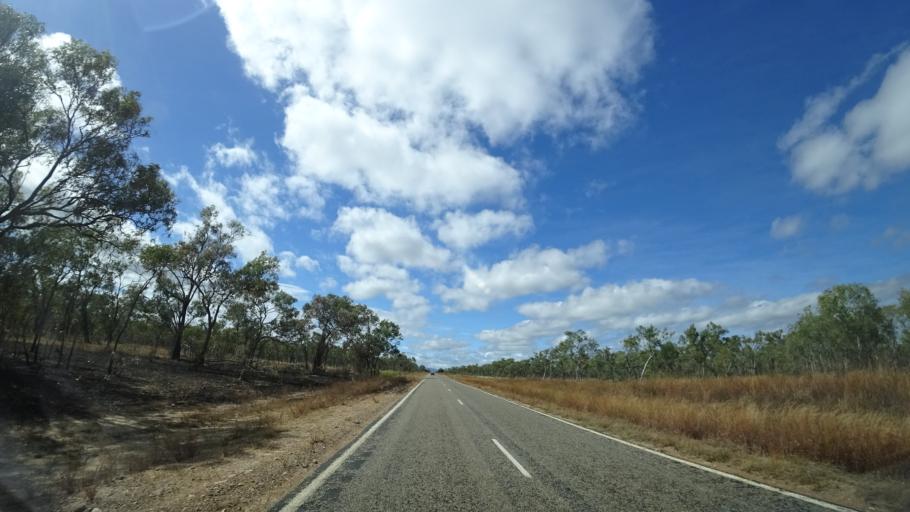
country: AU
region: Queensland
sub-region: Cairns
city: Port Douglas
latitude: -16.4894
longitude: 144.9223
